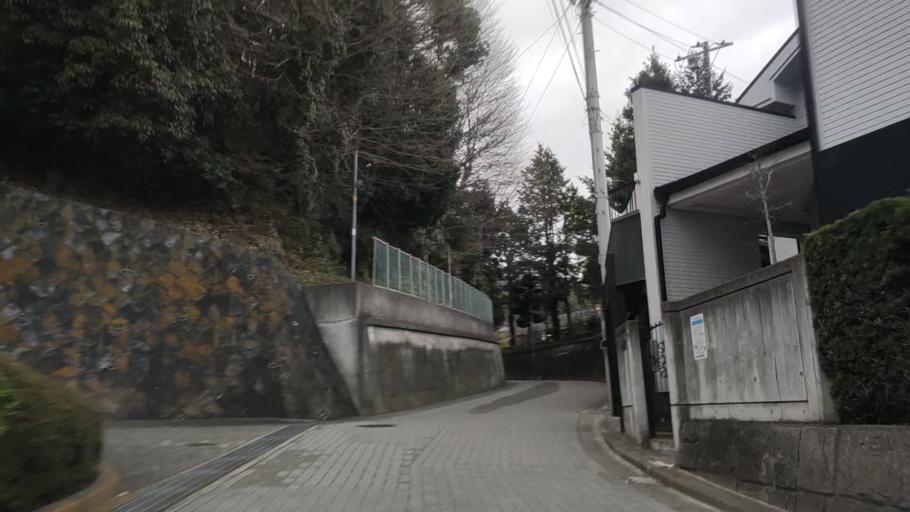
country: JP
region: Kanagawa
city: Oiso
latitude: 35.3105
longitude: 139.3145
